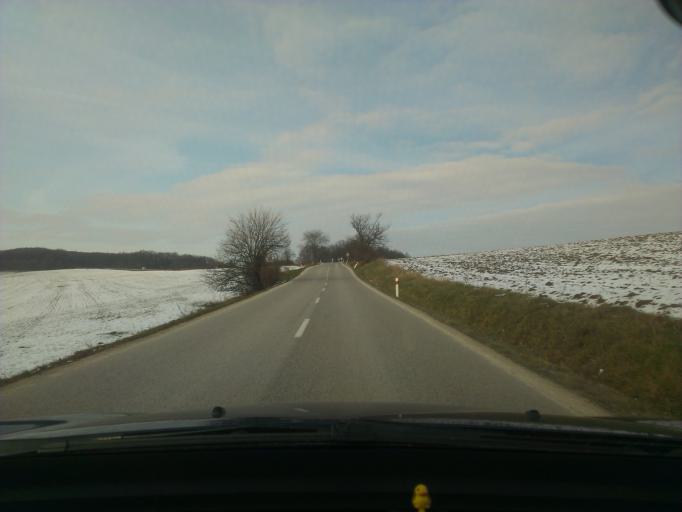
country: SK
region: Nitriansky
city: Stara Tura
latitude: 48.7148
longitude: 17.6856
